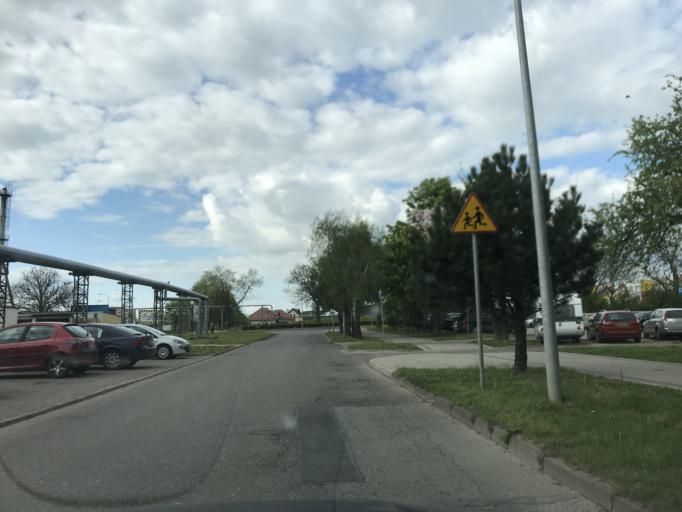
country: PL
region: West Pomeranian Voivodeship
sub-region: Powiat mysliborski
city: Mysliborz
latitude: 52.9265
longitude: 14.8776
